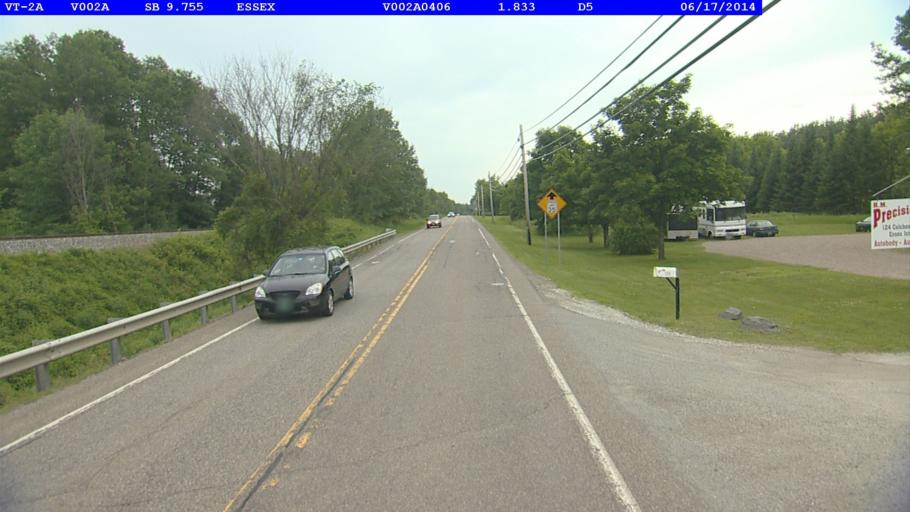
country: US
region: Vermont
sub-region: Chittenden County
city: Essex Junction
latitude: 44.5067
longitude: -73.1169
